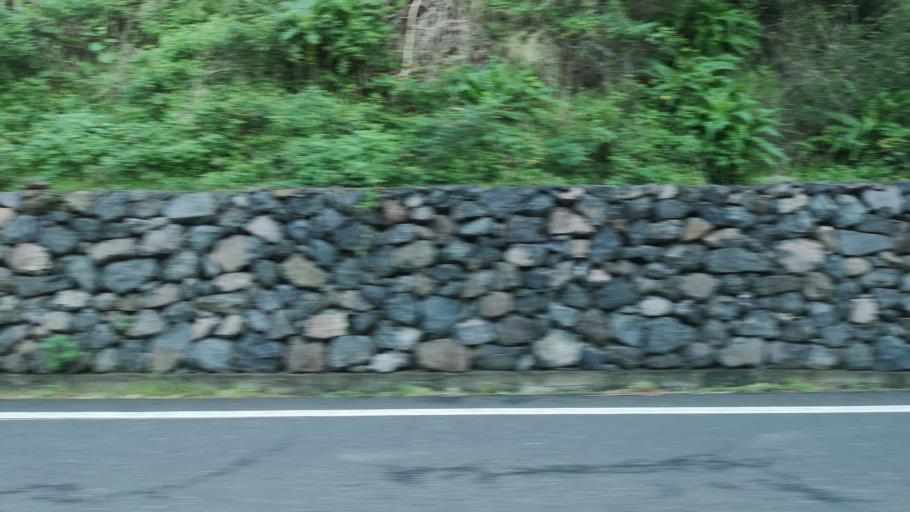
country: ES
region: Canary Islands
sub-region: Provincia de Santa Cruz de Tenerife
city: Hermigua
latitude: 28.1347
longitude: -17.1959
